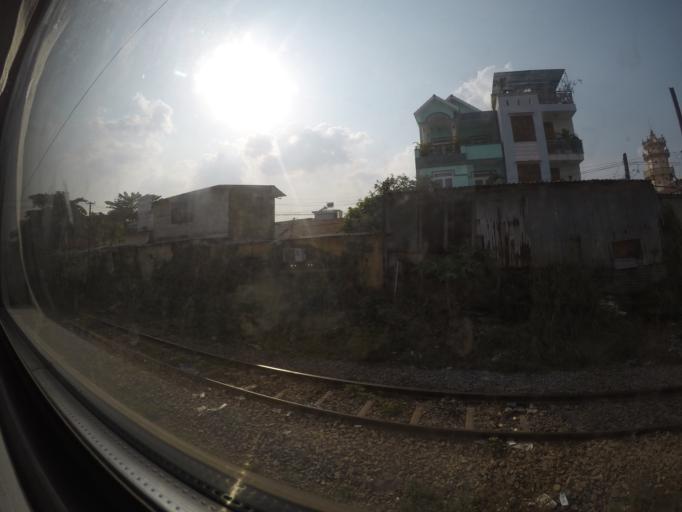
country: VN
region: Binh Duong
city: Di An
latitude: 10.9069
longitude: 106.7684
